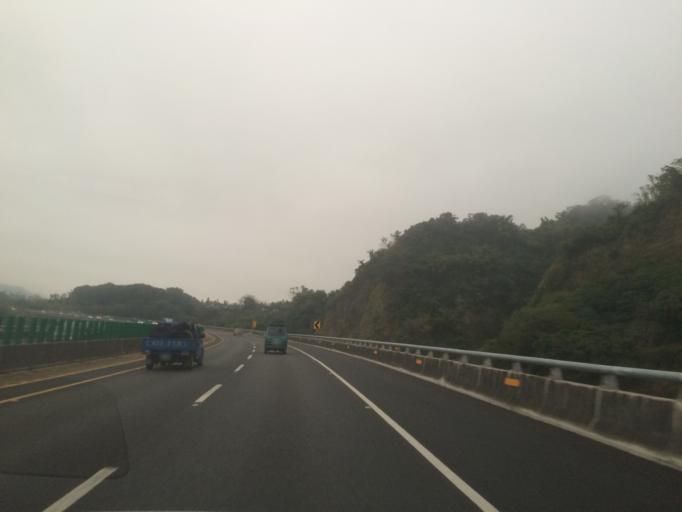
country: TW
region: Taiwan
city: Zhongxing New Village
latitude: 23.9888
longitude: 120.7854
